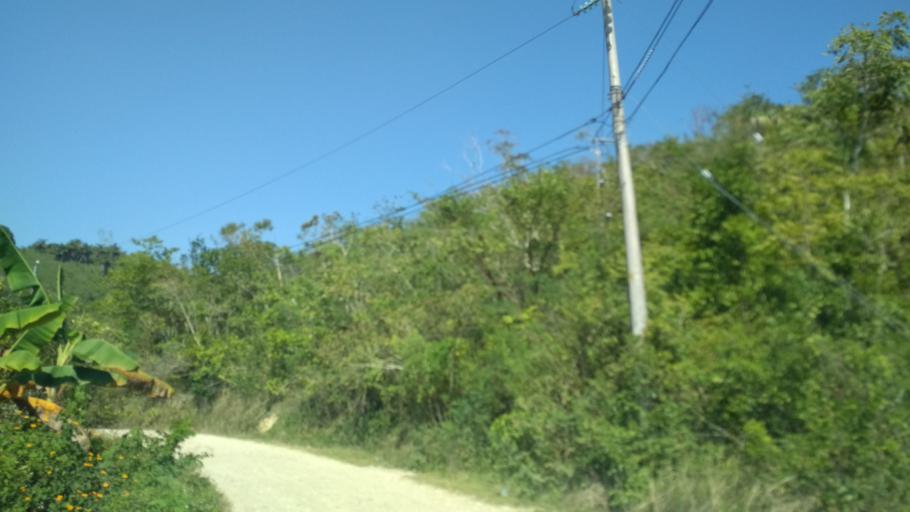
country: MX
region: Veracruz
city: Gutierrez Zamora
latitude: 20.4753
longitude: -97.1573
